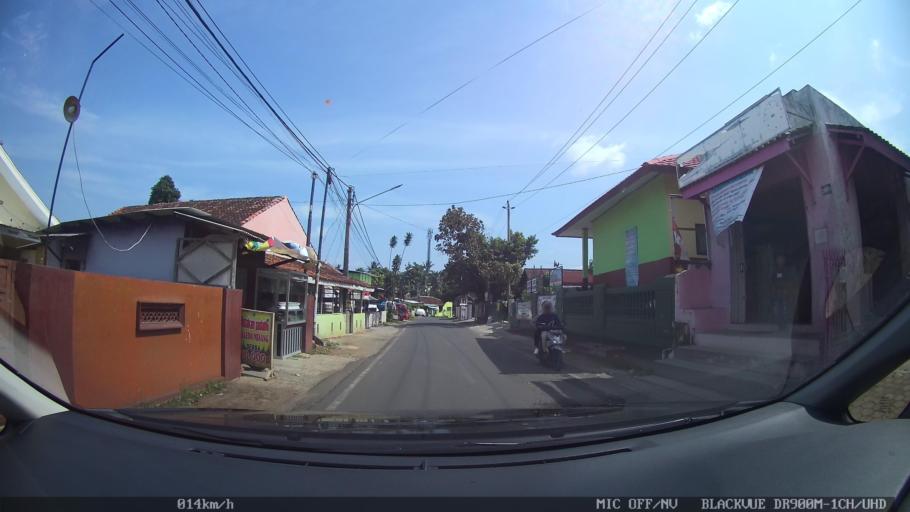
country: ID
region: Lampung
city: Kedaton
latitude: -5.3929
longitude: 105.2378
